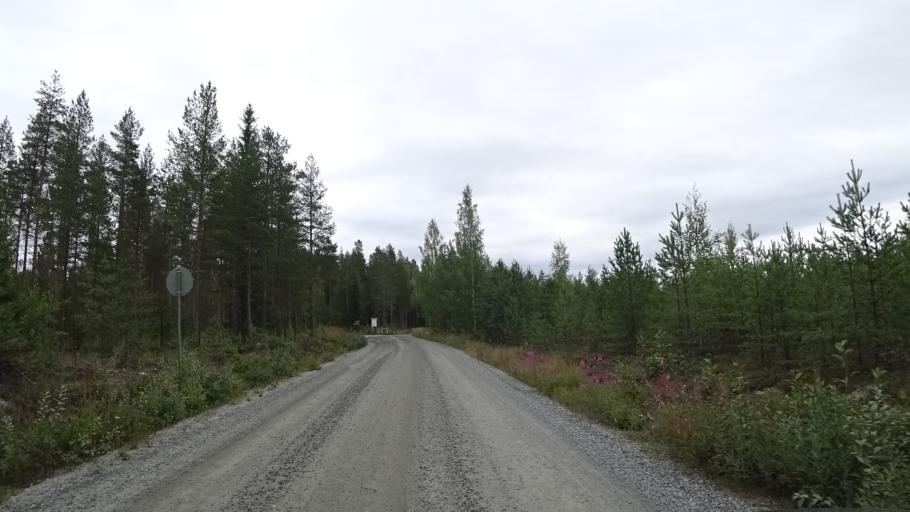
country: FI
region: North Karelia
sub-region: Pielisen Karjala
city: Lieksa
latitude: 63.3630
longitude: 30.3896
